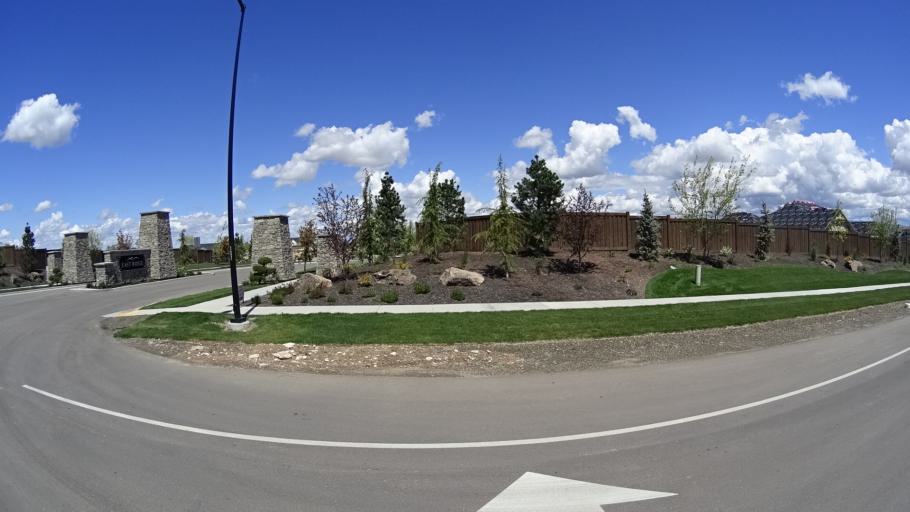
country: US
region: Idaho
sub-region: Ada County
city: Meridian
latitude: 43.5465
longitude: -116.3612
